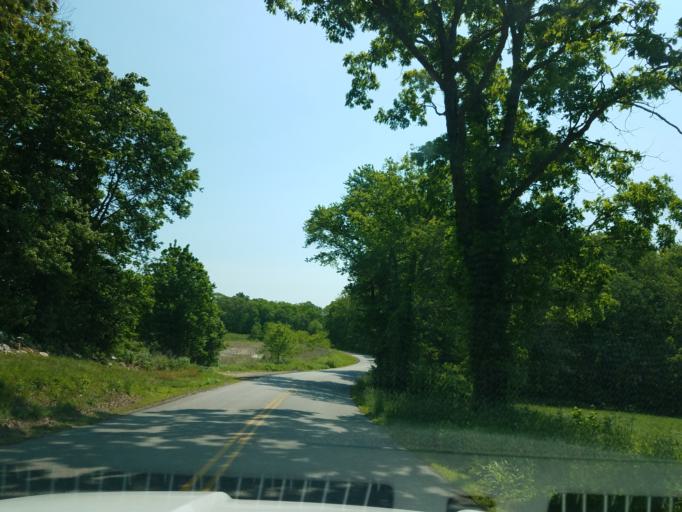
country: US
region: Connecticut
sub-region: New London County
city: Montville Center
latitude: 41.4971
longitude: -72.2210
